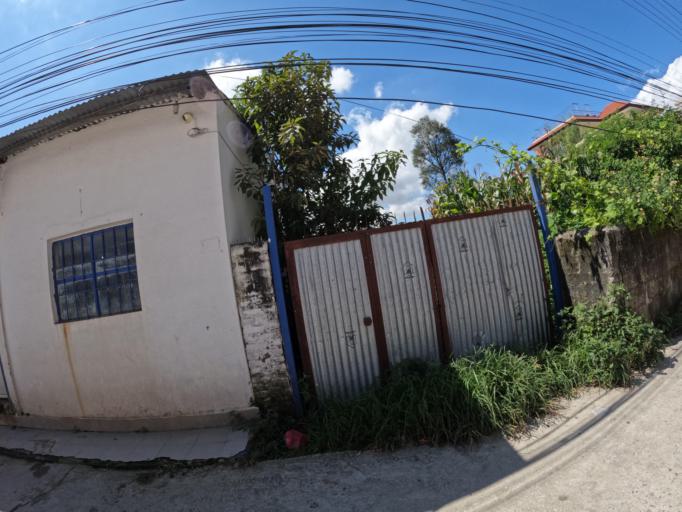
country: NP
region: Central Region
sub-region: Bagmati Zone
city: Kathmandu
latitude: 27.7547
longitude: 85.3286
